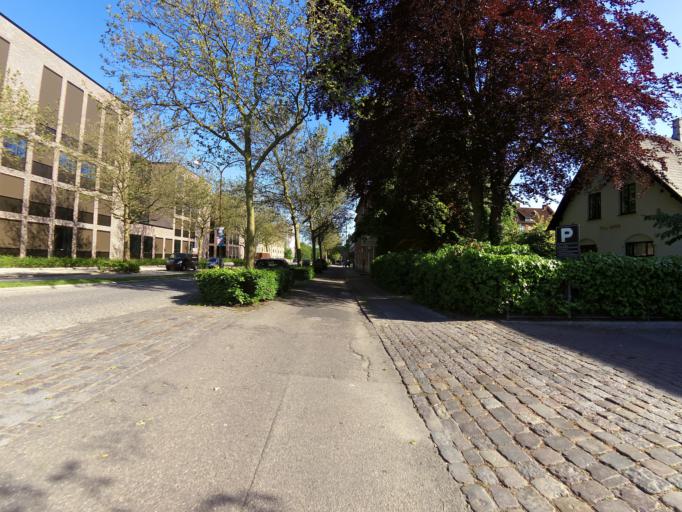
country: DK
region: Capital Region
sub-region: Lyngby-Tarbaek Kommune
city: Kongens Lyngby
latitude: 55.7653
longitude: 12.5096
